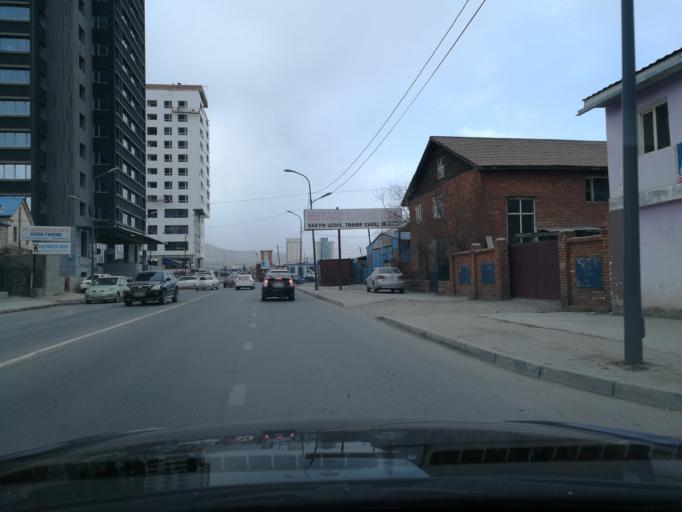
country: MN
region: Ulaanbaatar
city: Ulaanbaatar
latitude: 47.9316
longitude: 106.9138
